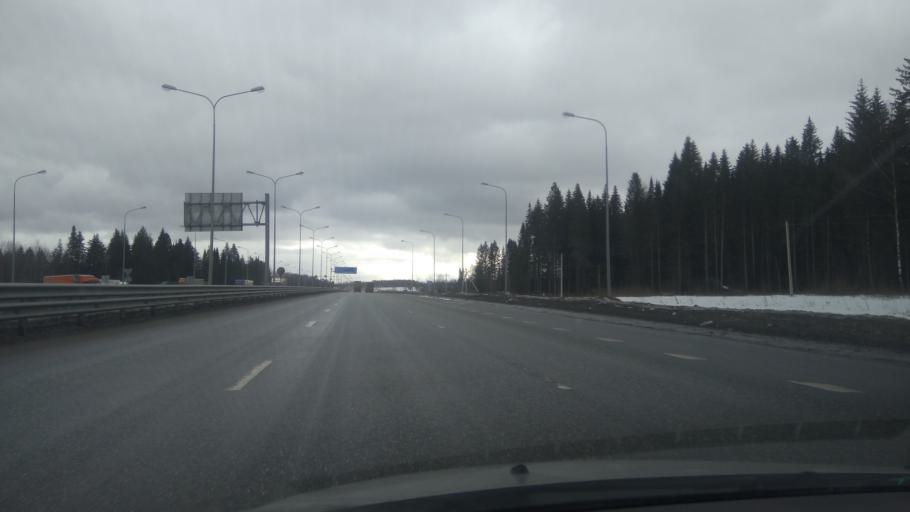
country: RU
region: Perm
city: Bershet'
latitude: 57.6945
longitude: 56.3915
